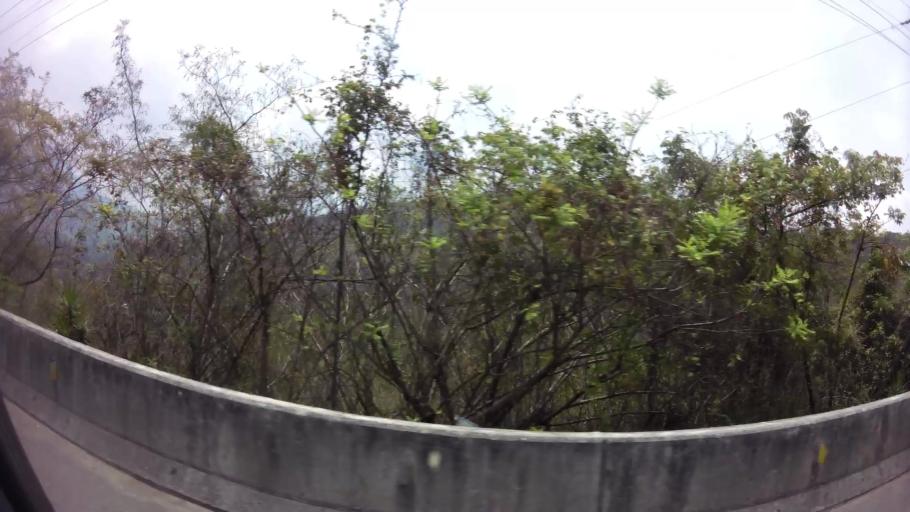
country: HN
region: Comayagua
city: Taulabe
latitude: 14.6890
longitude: -87.9456
